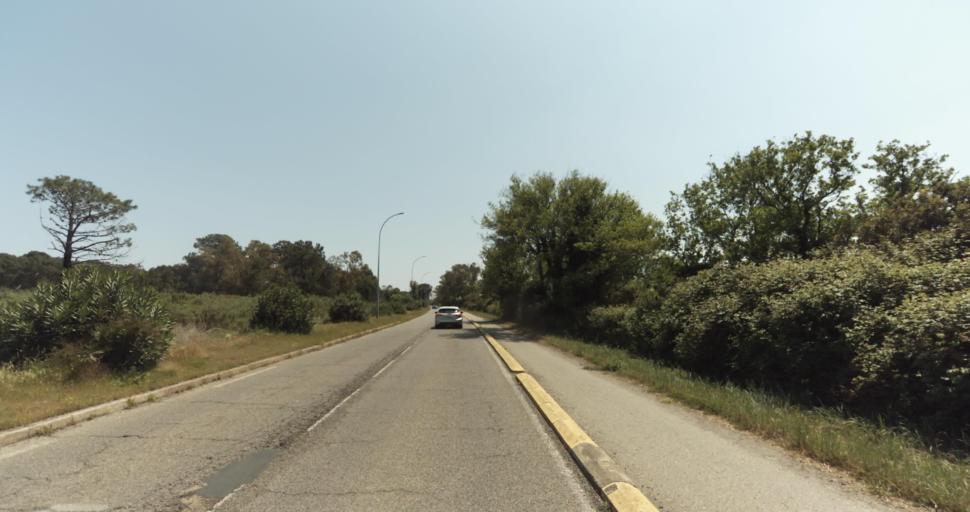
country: FR
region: Corsica
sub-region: Departement de la Haute-Corse
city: Biguglia
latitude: 42.6482
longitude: 9.4531
